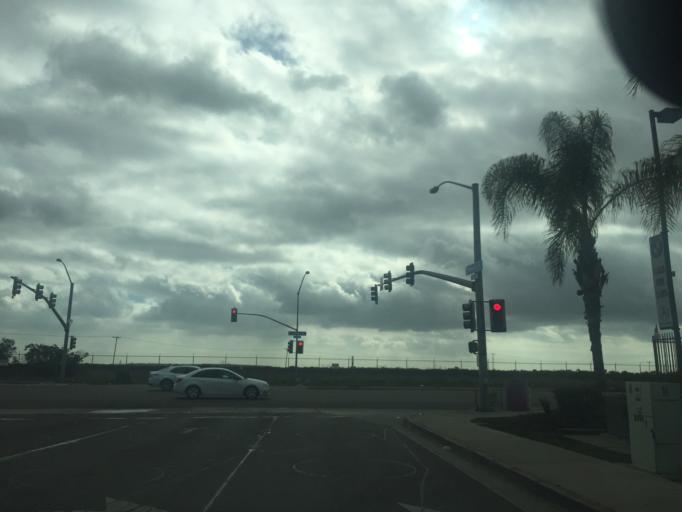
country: US
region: California
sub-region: San Diego County
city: La Jolla
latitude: 32.8780
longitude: -117.1785
